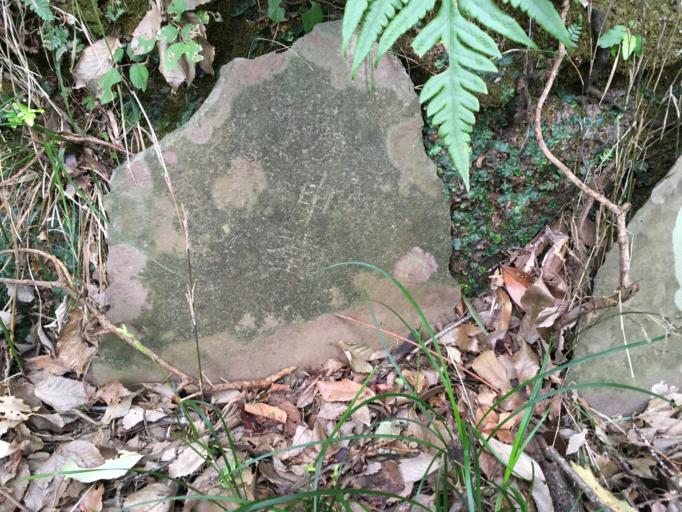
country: JP
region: Kanagawa
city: Kamakura
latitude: 35.3177
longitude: 139.5712
